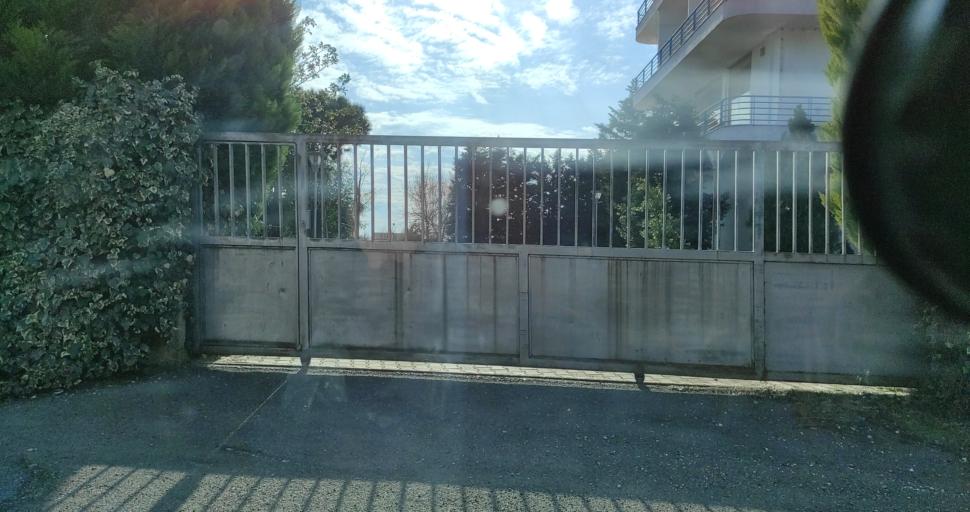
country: AL
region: Lezhe
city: Lezhe
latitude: 41.7818
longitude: 19.6308
